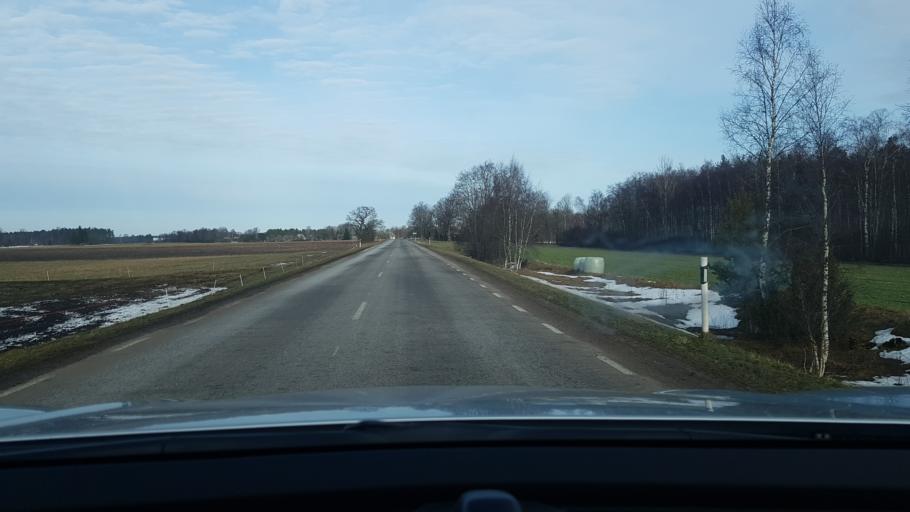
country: EE
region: Saare
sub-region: Kuressaare linn
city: Kuressaare
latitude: 58.4983
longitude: 22.7063
